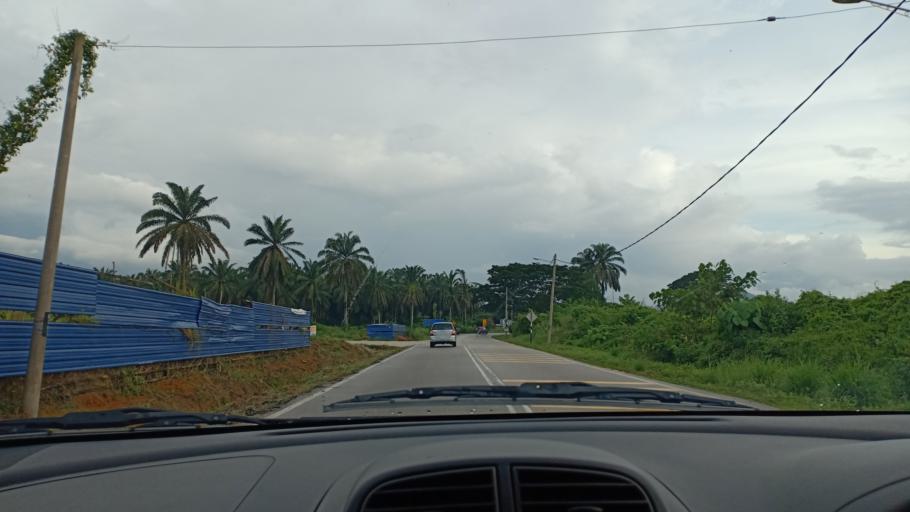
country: MY
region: Penang
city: Tasek Glugor
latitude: 5.4406
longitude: 100.5129
